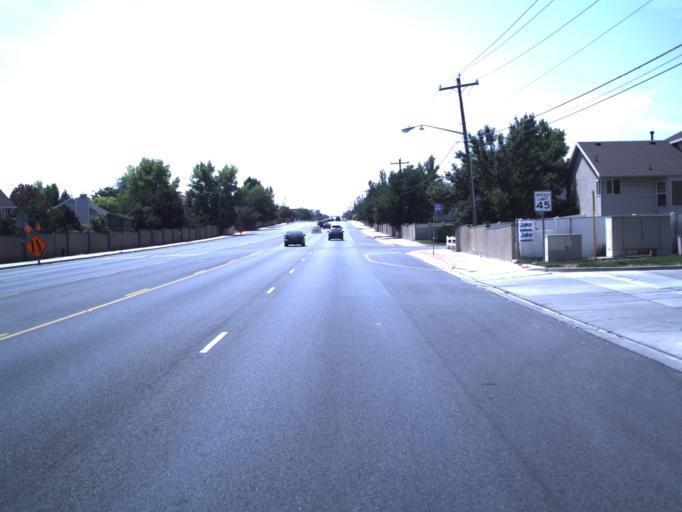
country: US
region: Utah
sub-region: Salt Lake County
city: West Valley City
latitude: 40.6779
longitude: -112.0248
